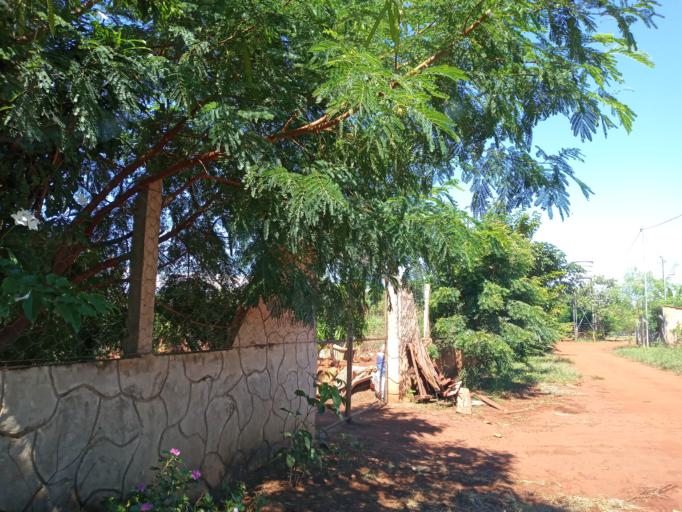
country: BR
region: Goias
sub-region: Itumbiara
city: Itumbiara
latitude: -18.4303
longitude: -49.1173
